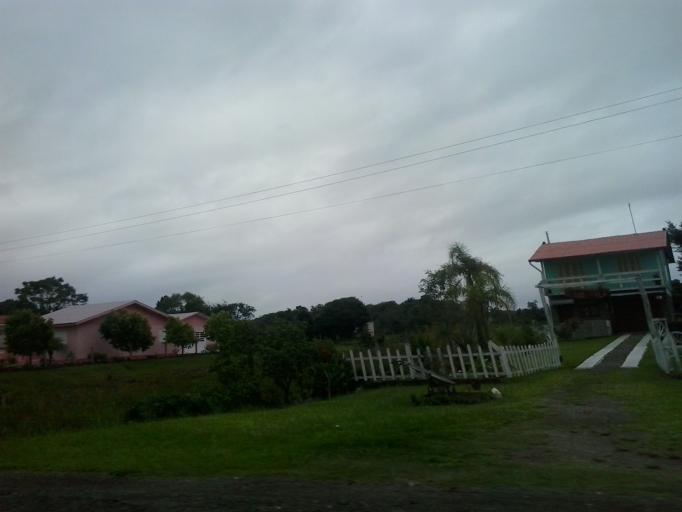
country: BR
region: Rio Grande do Sul
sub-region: Santa Maria
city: Santa Maria
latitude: -29.7223
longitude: -53.3783
